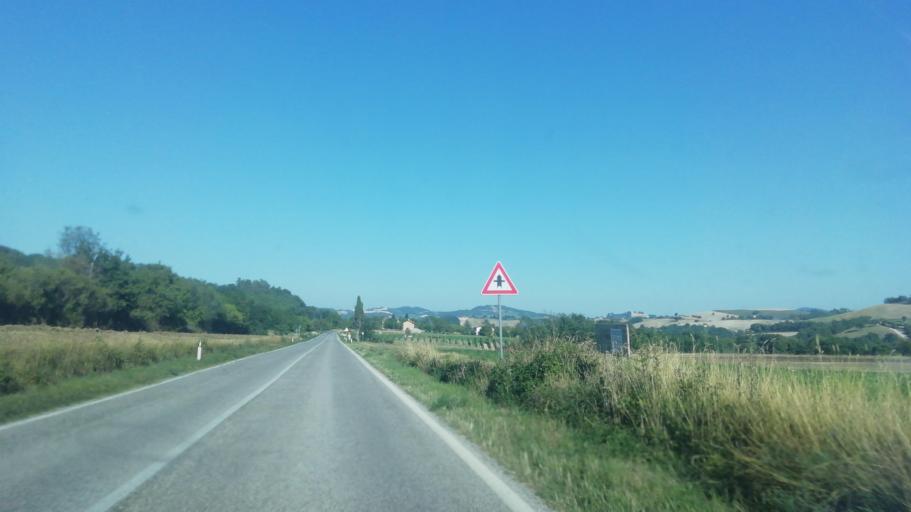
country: IT
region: The Marches
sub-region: Provincia di Pesaro e Urbino
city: Frontone
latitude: 43.5465
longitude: 12.7792
